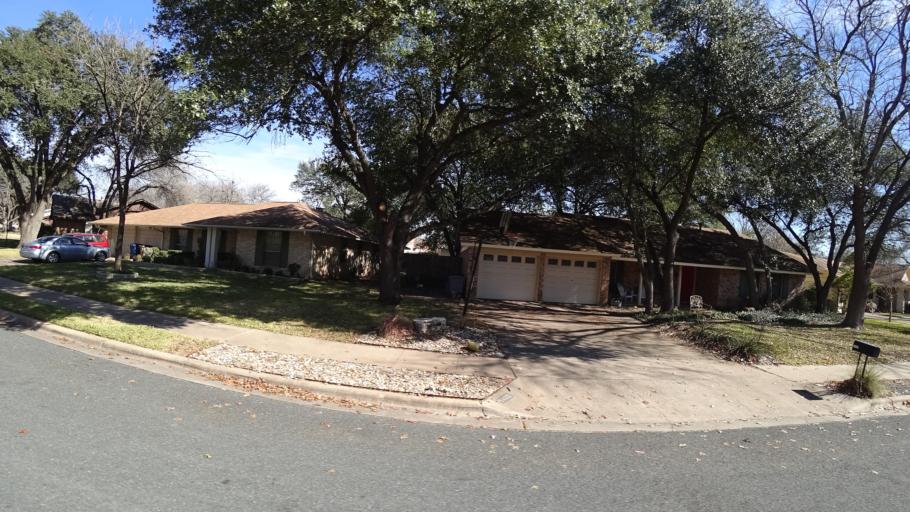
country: US
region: Texas
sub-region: Travis County
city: Wells Branch
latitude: 30.3786
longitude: -97.7016
